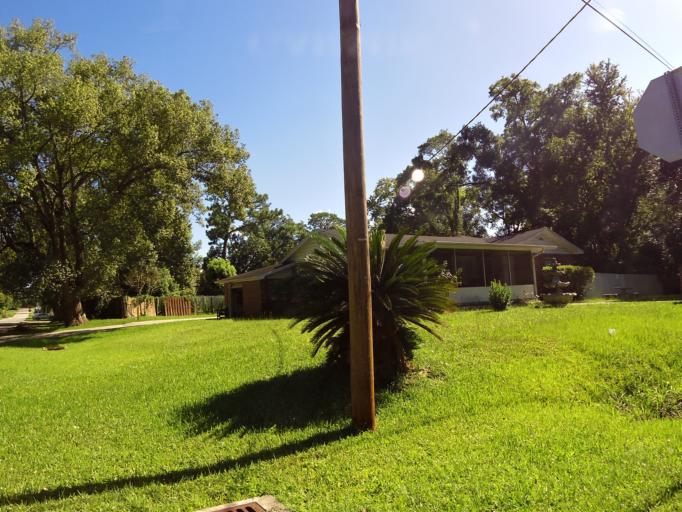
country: US
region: Florida
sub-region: Duval County
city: Jacksonville
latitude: 30.2805
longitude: -81.7241
